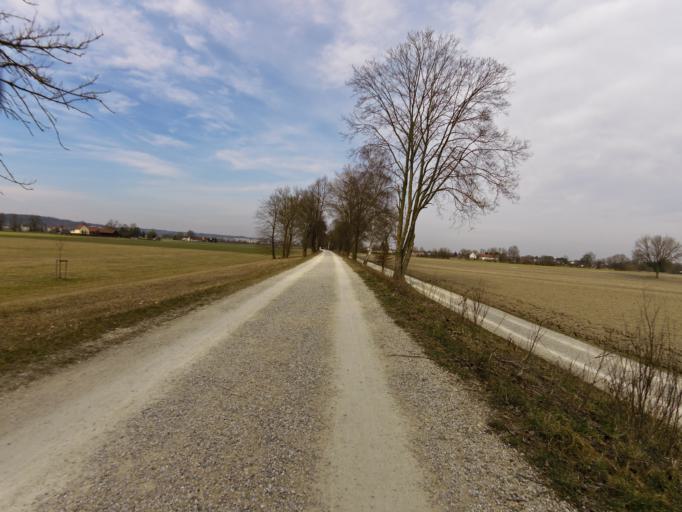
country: DE
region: Bavaria
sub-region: Lower Bavaria
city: Tiefenbach
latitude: 48.5289
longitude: 12.1093
